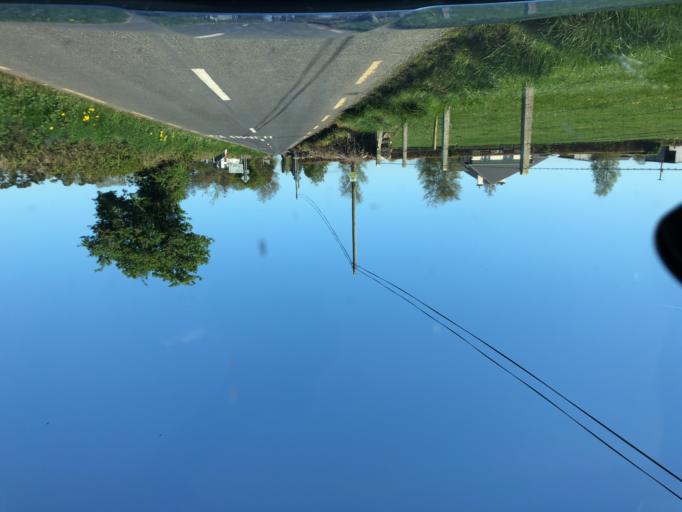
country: IE
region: Connaught
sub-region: County Galway
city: Portumna
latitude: 53.1764
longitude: -8.1994
